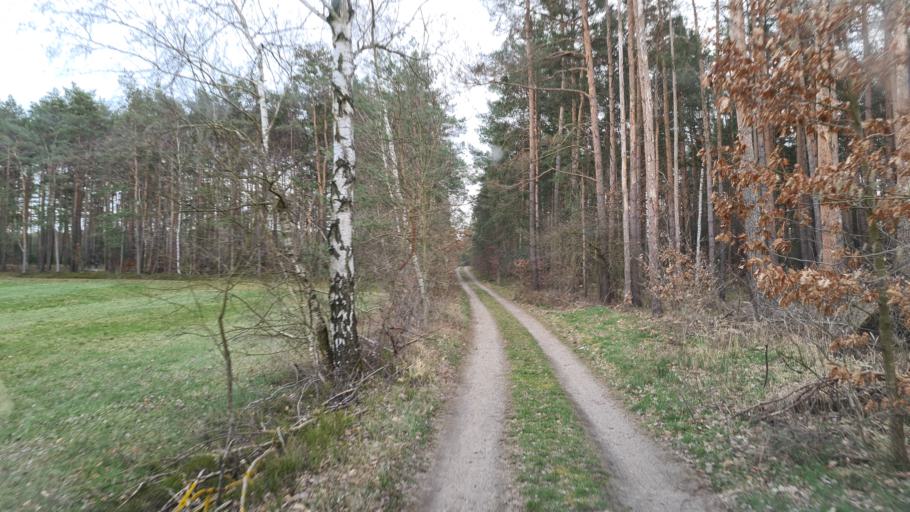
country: DE
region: Brandenburg
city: Schonborn
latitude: 51.5523
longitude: 13.4938
